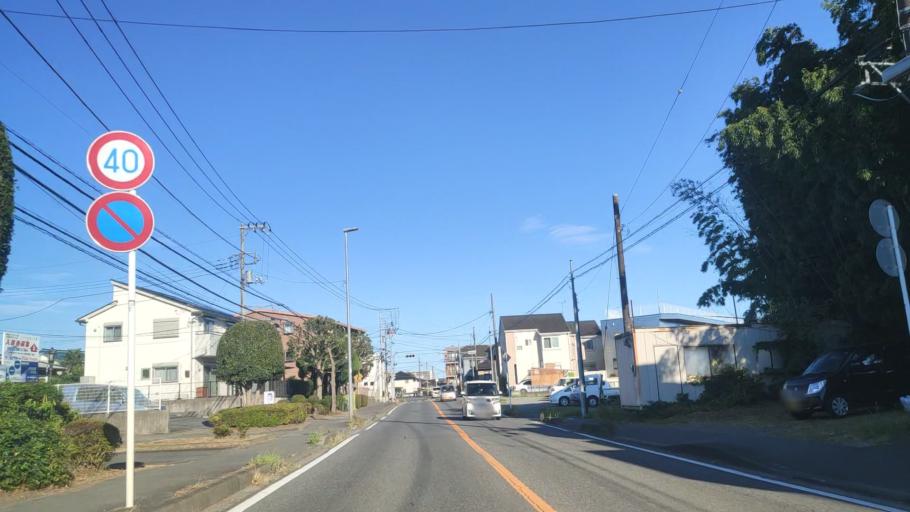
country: JP
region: Tokyo
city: Hachioji
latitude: 35.5852
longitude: 139.3215
